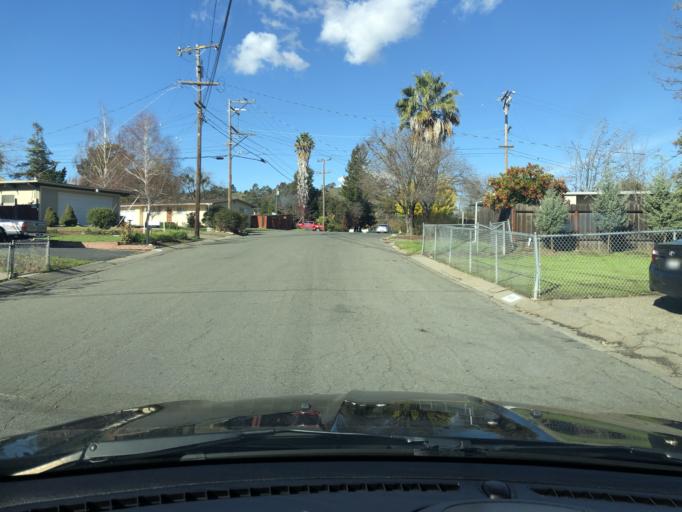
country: US
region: California
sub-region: Contra Costa County
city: Pacheco
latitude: 37.9896
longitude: -122.0734
